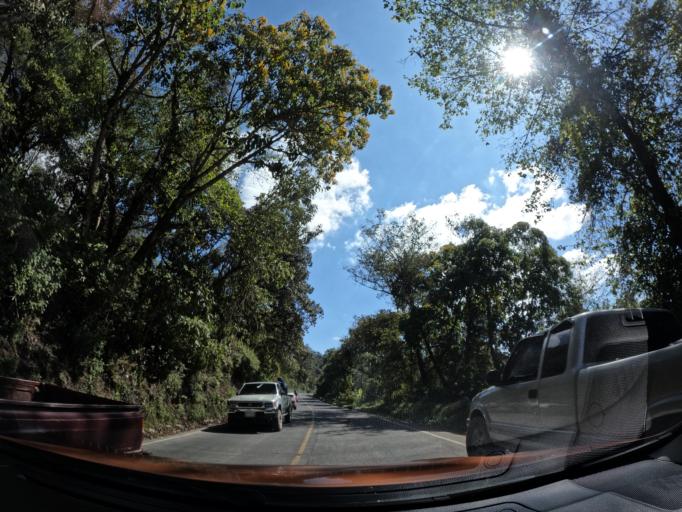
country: GT
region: Chimaltenango
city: Patzun
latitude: 14.6511
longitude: -91.0470
